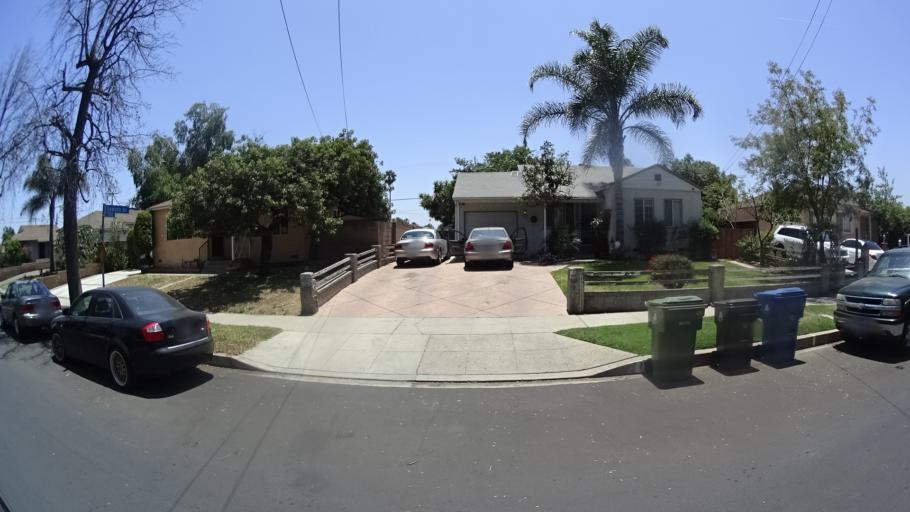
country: US
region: California
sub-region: Los Angeles County
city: Van Nuys
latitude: 34.2149
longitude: -118.4602
